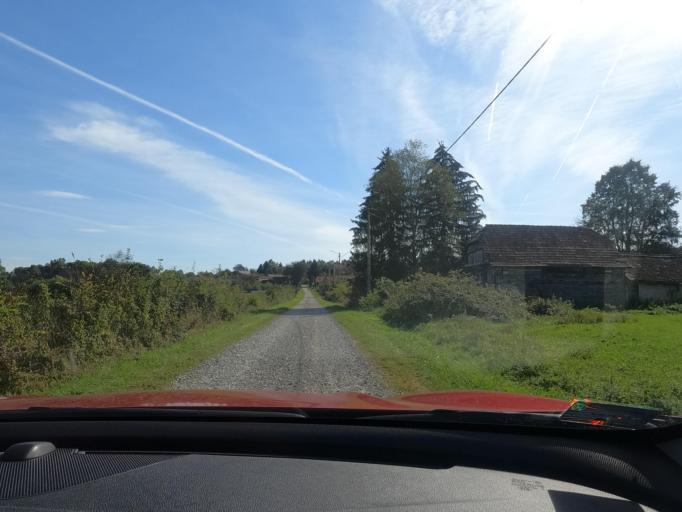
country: HR
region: Sisacko-Moslavacka
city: Petrinja
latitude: 45.3420
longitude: 16.2332
